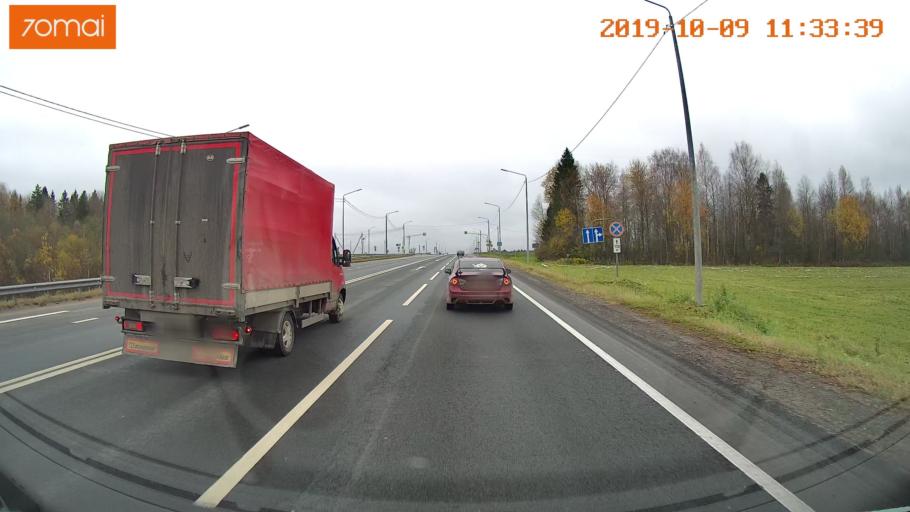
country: RU
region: Vologda
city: Gryazovets
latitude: 59.0229
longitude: 40.1148
